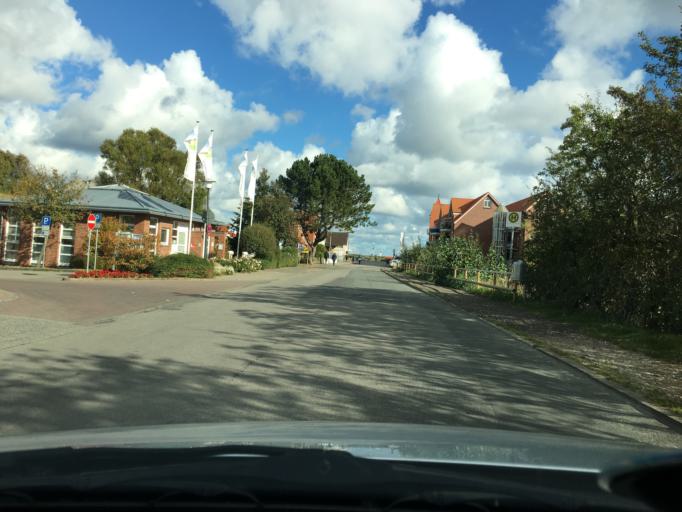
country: DE
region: Schleswig-Holstein
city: Krummbek
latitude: 54.4122
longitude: 10.4147
